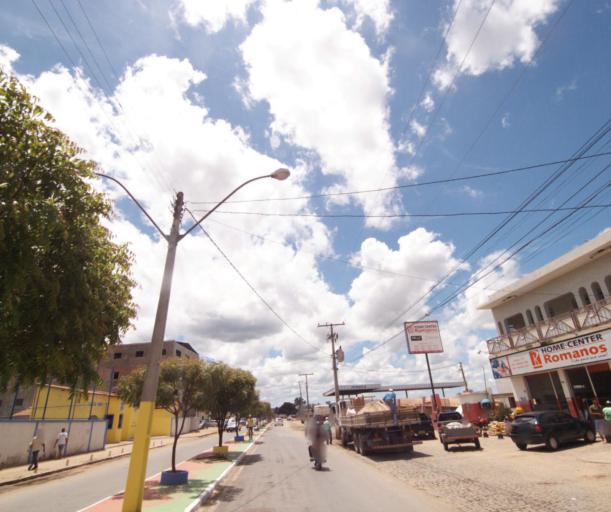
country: BR
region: Bahia
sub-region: Bom Jesus Da Lapa
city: Bom Jesus da Lapa
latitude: -13.2655
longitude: -43.4105
